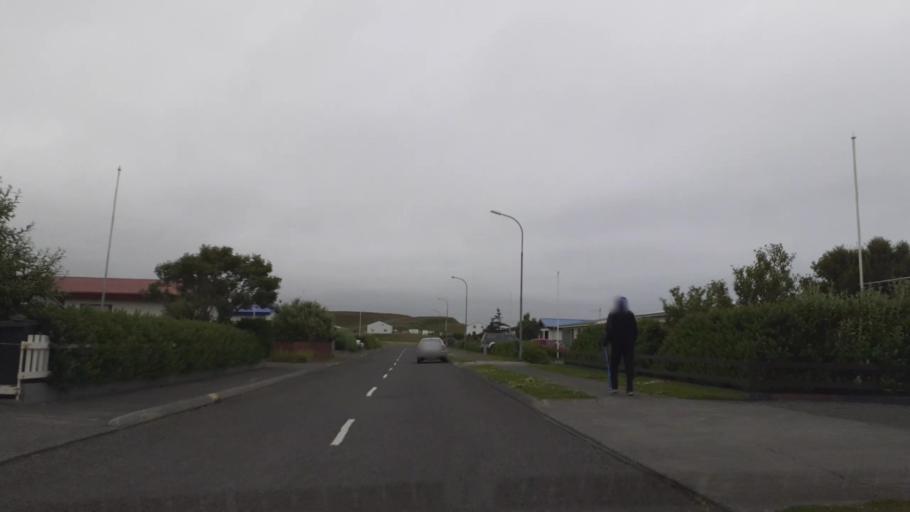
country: IS
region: Northwest
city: Saudarkrokur
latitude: 65.6572
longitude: -20.3043
